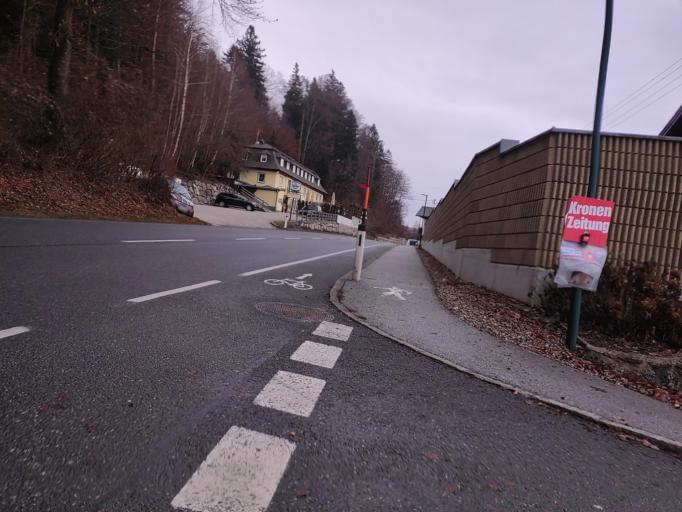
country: AT
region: Salzburg
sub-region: Politischer Bezirk Salzburg-Umgebung
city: Obertrum am See
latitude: 47.9311
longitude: 13.0878
